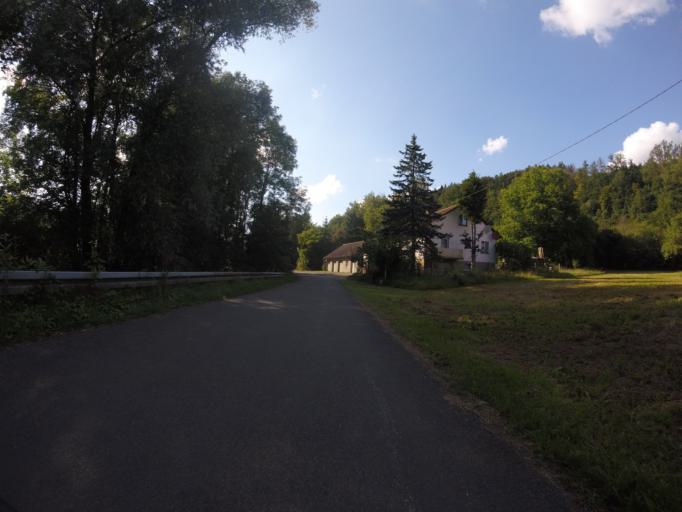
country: DE
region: Baden-Wuerttemberg
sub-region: Regierungsbezirk Stuttgart
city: Murrhardt
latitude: 48.9739
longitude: 9.6145
